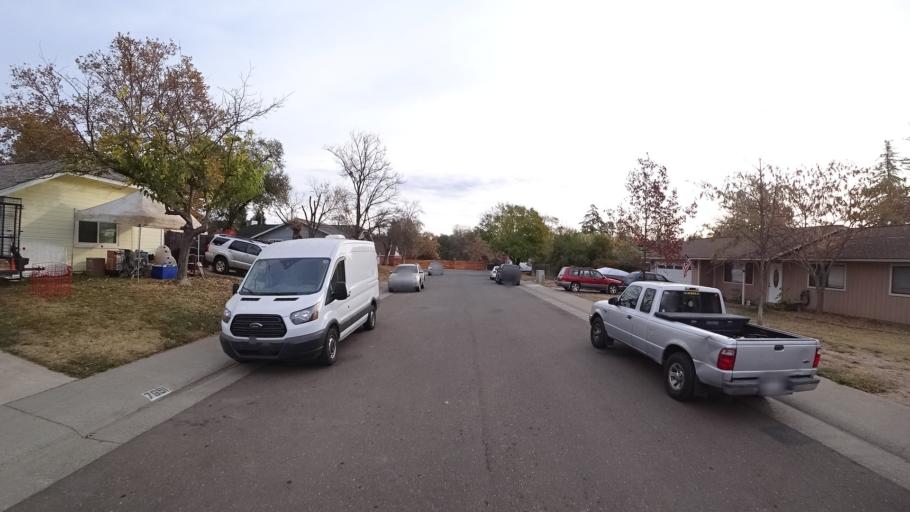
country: US
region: California
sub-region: Sacramento County
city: Citrus Heights
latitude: 38.7162
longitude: -121.2820
